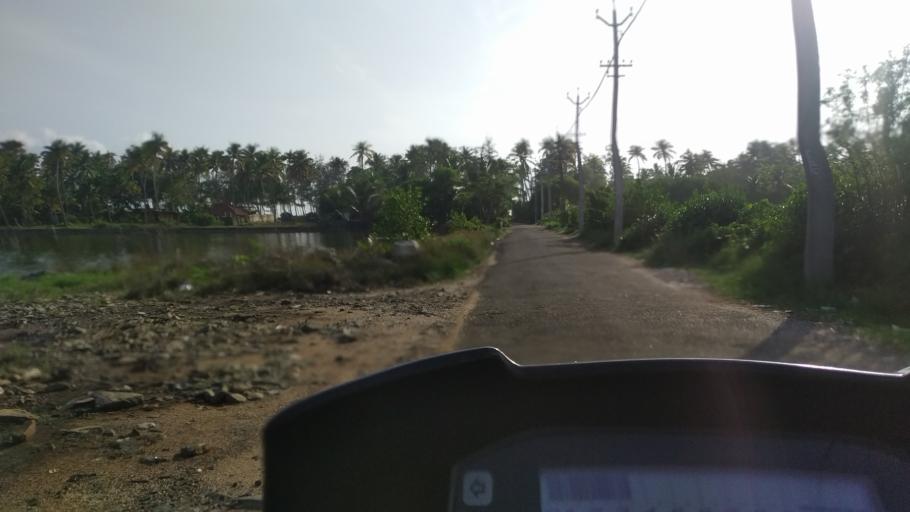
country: IN
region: Kerala
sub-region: Thrissur District
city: Kodungallur
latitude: 10.1278
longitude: 76.1848
